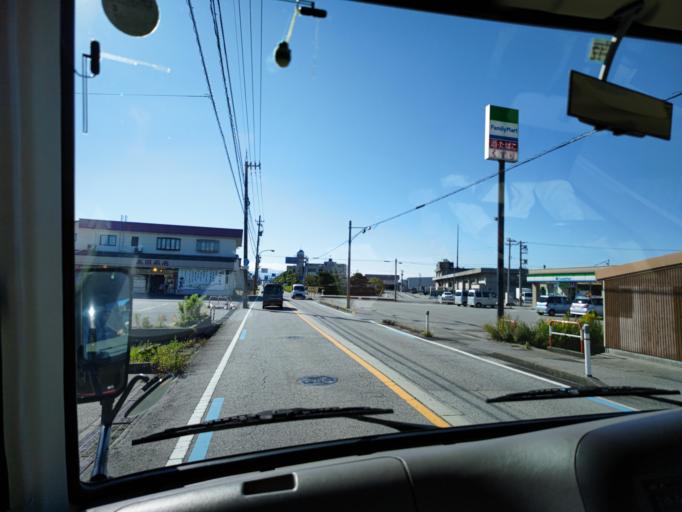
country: JP
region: Toyama
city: Nyuzen
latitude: 36.8940
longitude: 137.4195
